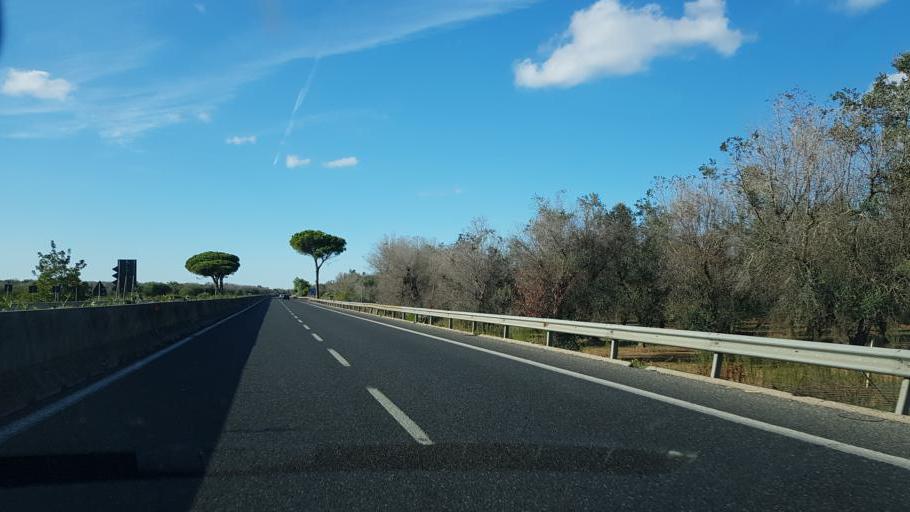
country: IT
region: Apulia
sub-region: Provincia di Brindisi
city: Torchiarolo
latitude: 40.4640
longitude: 18.0569
